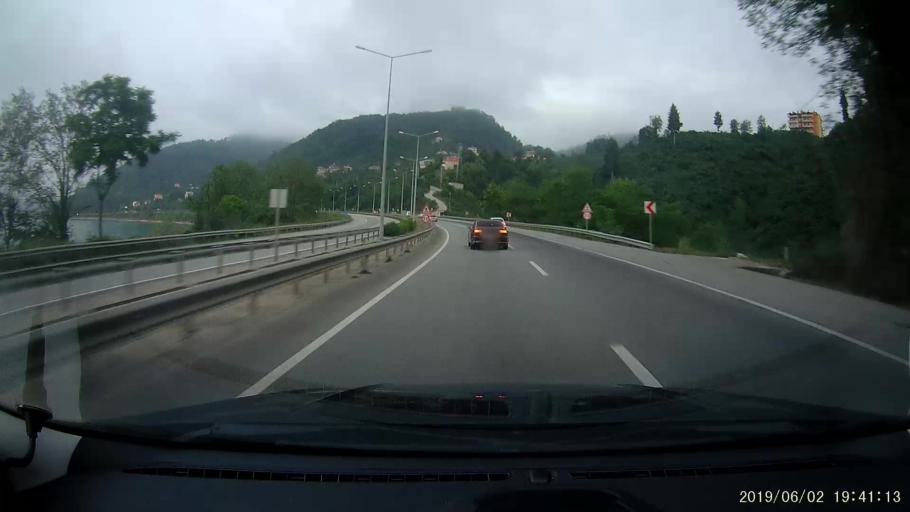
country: TR
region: Giresun
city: Kesap
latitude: 40.9152
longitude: 38.4757
